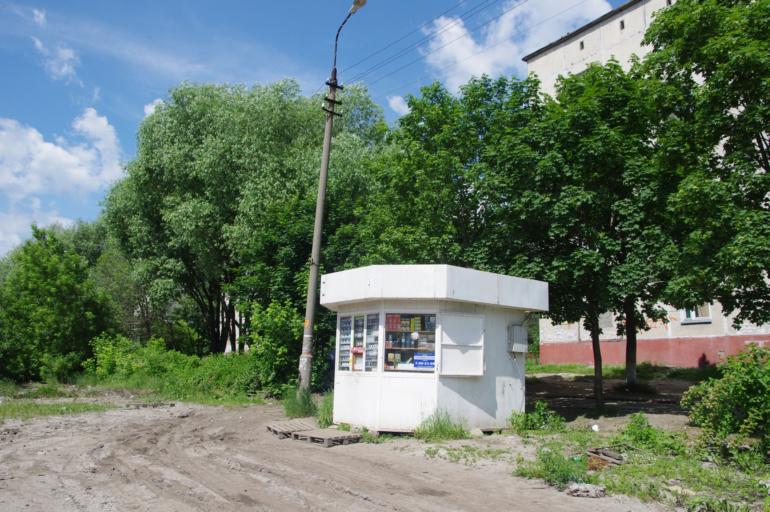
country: RU
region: Moskovskaya
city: Malyshevo
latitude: 55.5397
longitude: 38.3083
